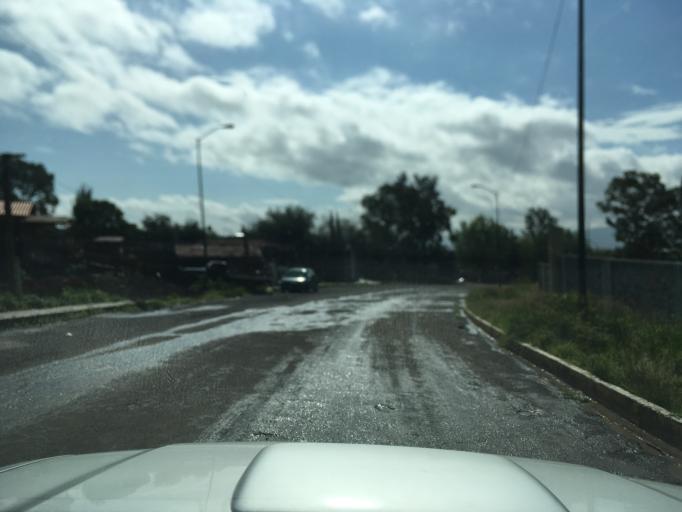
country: MX
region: Michoacan
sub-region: Tarimbaro
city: Fraccionamiento Metropolis II
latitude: 19.7215
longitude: -101.2331
